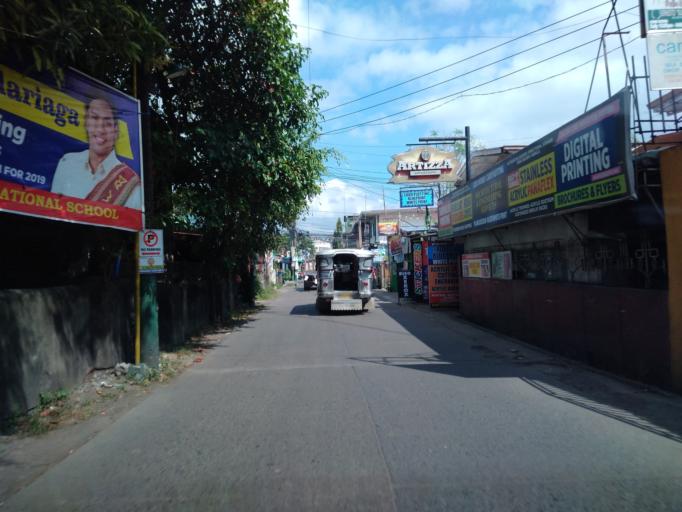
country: PH
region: Central Luzon
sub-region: Province of Bulacan
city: Santa Maria
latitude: 14.8219
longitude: 120.9631
